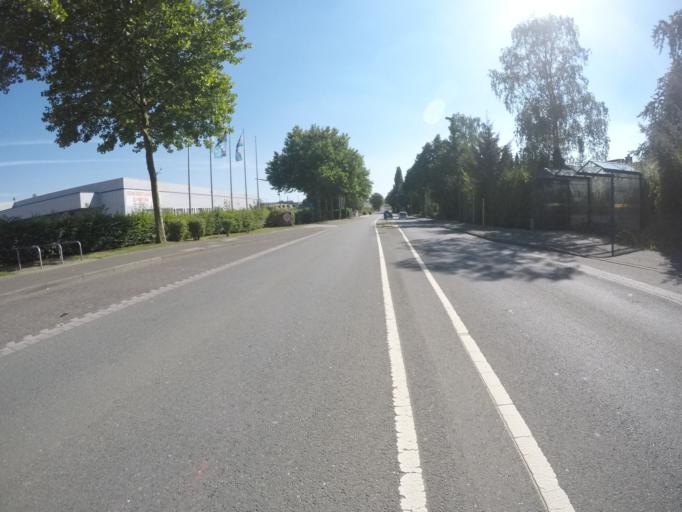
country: DE
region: North Rhine-Westphalia
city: Bad Oeynhausen
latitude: 52.1794
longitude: 8.7530
